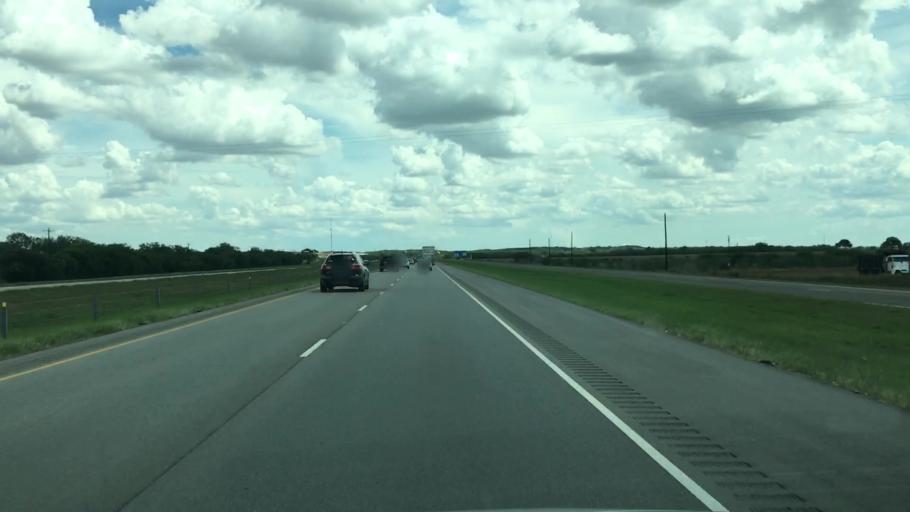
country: US
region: Texas
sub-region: Live Oak County
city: George West
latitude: 28.2713
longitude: -97.9445
